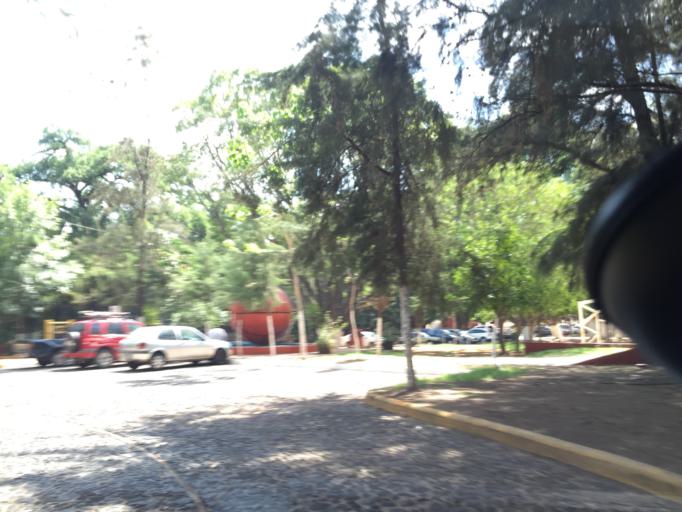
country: MX
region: Jalisco
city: Atotonilco el Alto
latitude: 20.5639
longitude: -102.4775
